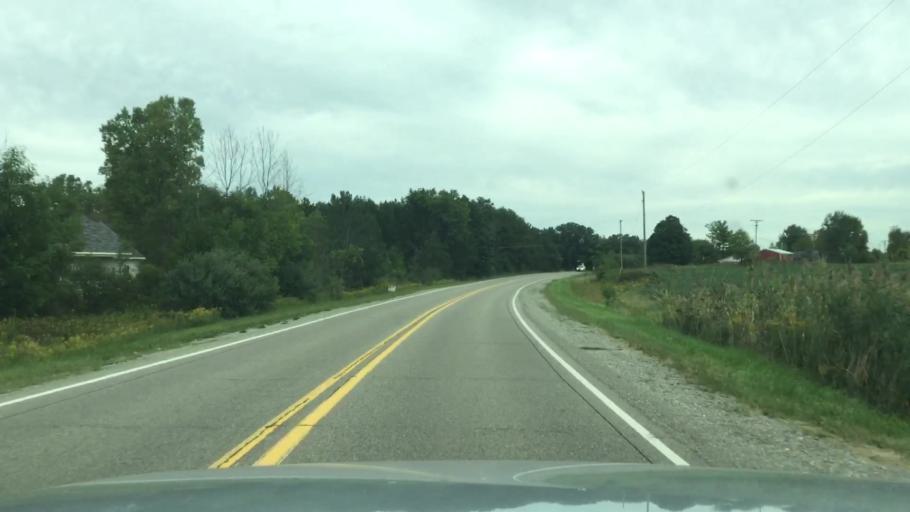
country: US
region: Michigan
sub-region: Shiawassee County
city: Durand
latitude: 42.9554
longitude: -83.9234
